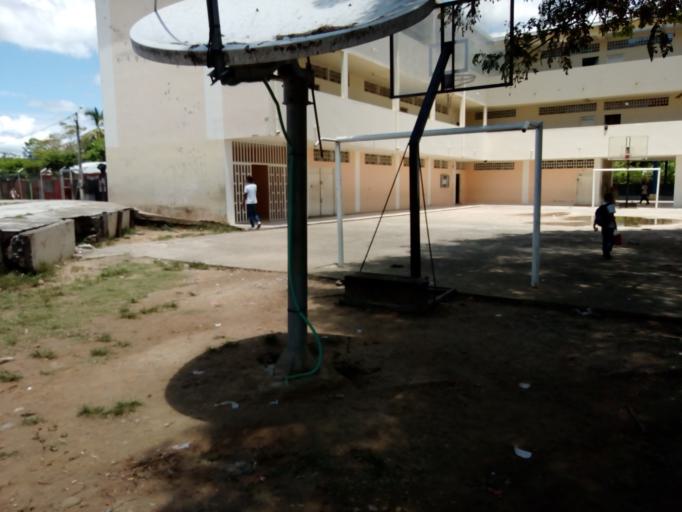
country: CO
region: Boyaca
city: Puerto Boyaca
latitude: 6.0668
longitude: -74.2682
